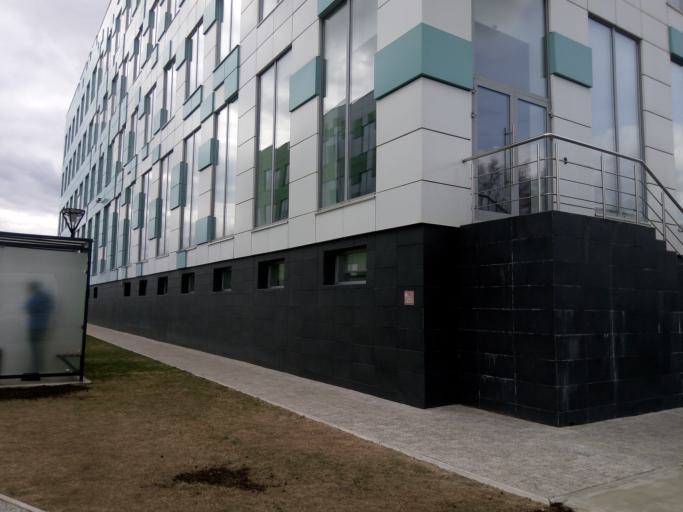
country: RU
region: Moskovskaya
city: Skolkovo
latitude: 55.6849
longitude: 37.3421
